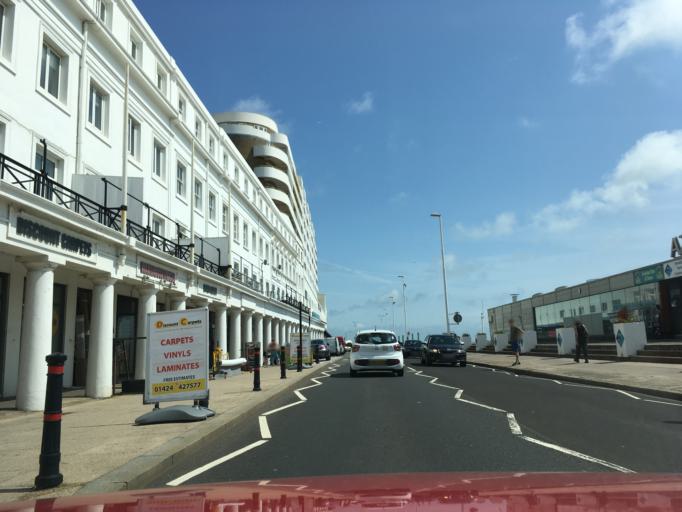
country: GB
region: England
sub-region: East Sussex
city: Saint Leonards-on-Sea
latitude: 50.8509
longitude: 0.5550
